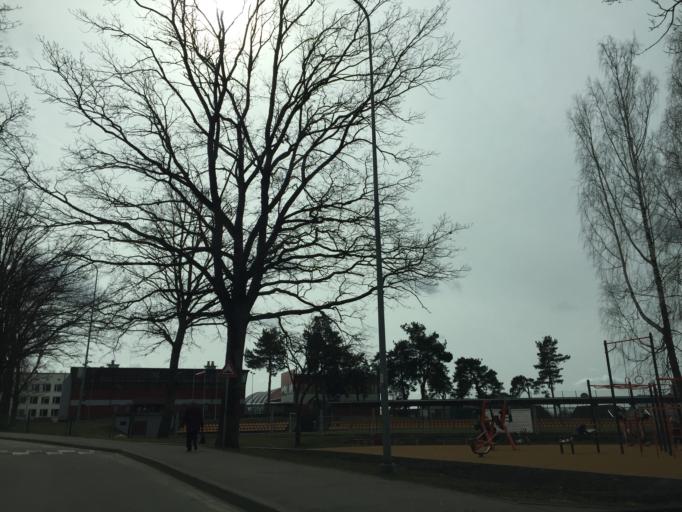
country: LV
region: Livani
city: Livani
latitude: 56.3597
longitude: 26.1712
